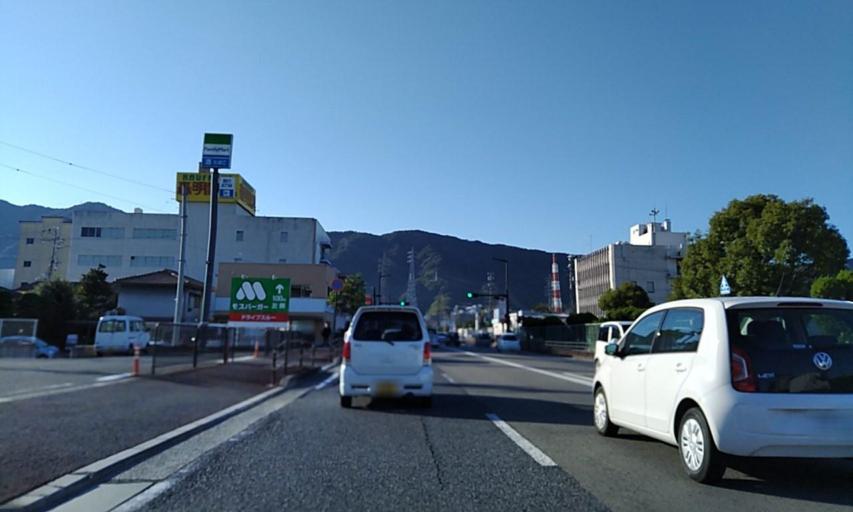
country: JP
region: Wakayama
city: Kainan
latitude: 34.1554
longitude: 135.2055
